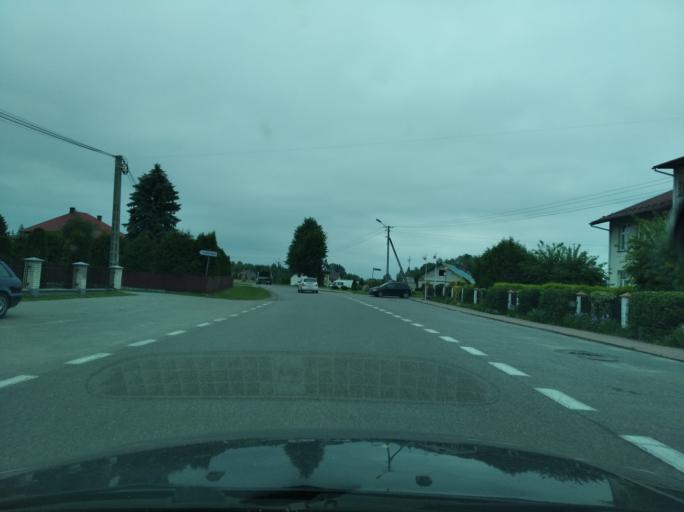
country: PL
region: Subcarpathian Voivodeship
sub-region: Powiat kolbuszowski
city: Niwiska
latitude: 50.1549
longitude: 21.6704
